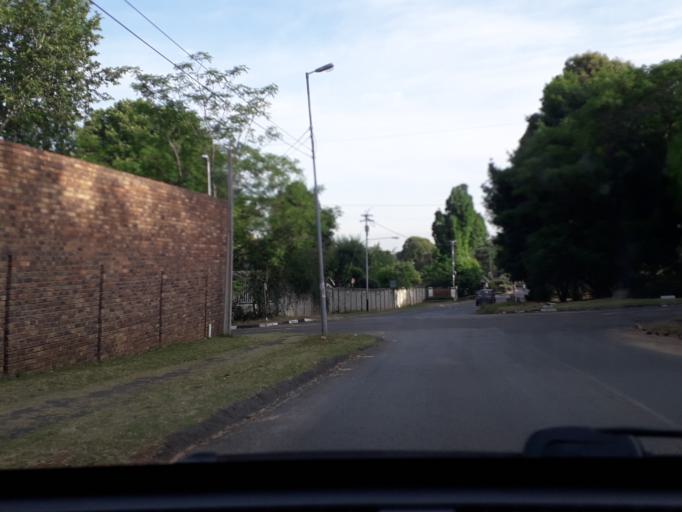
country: ZA
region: Gauteng
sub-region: City of Johannesburg Metropolitan Municipality
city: Johannesburg
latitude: -26.1215
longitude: 28.0759
